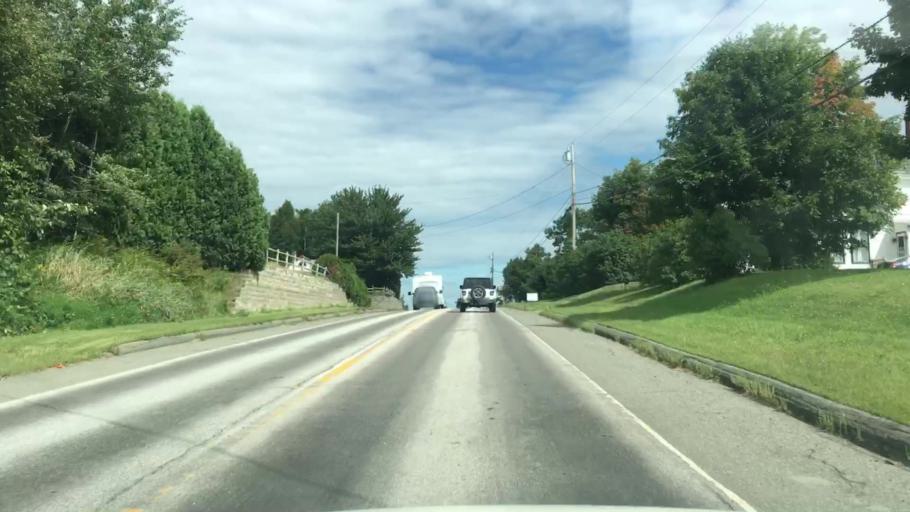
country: US
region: Maine
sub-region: Piscataquis County
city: Dover-Foxcroft
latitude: 45.1628
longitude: -69.2313
